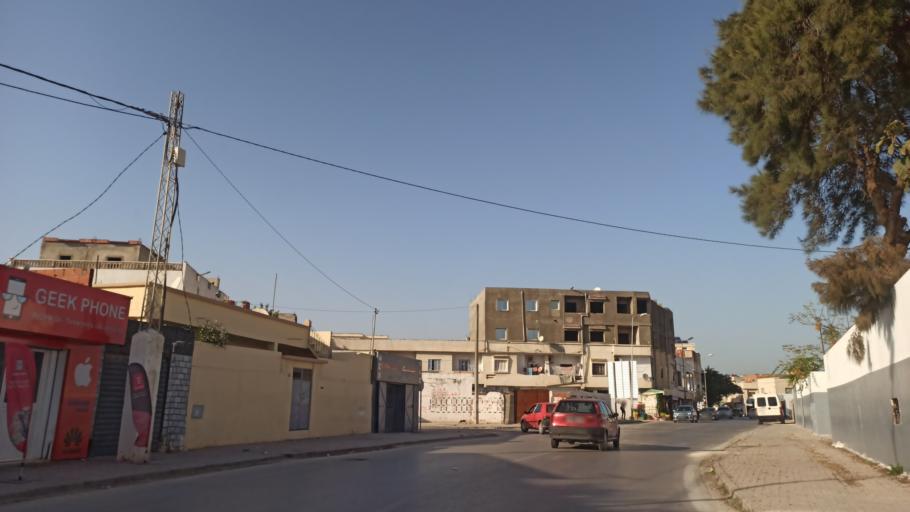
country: TN
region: Tunis
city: La Goulette
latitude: 36.8544
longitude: 10.2721
